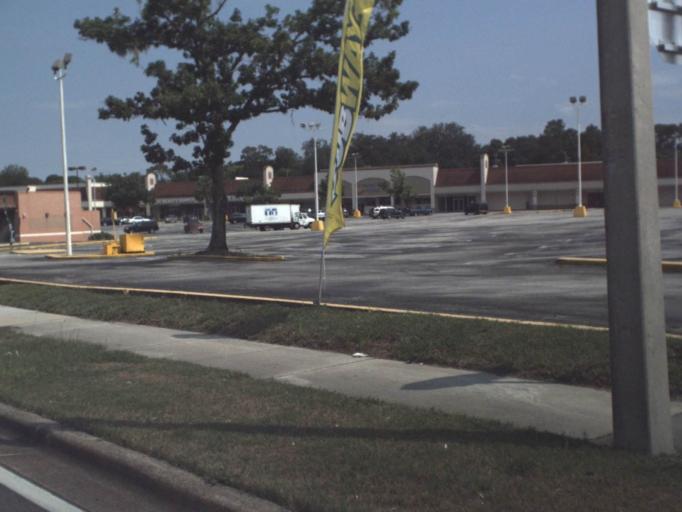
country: US
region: Florida
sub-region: Duval County
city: Jacksonville
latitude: 30.3030
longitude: -81.6293
